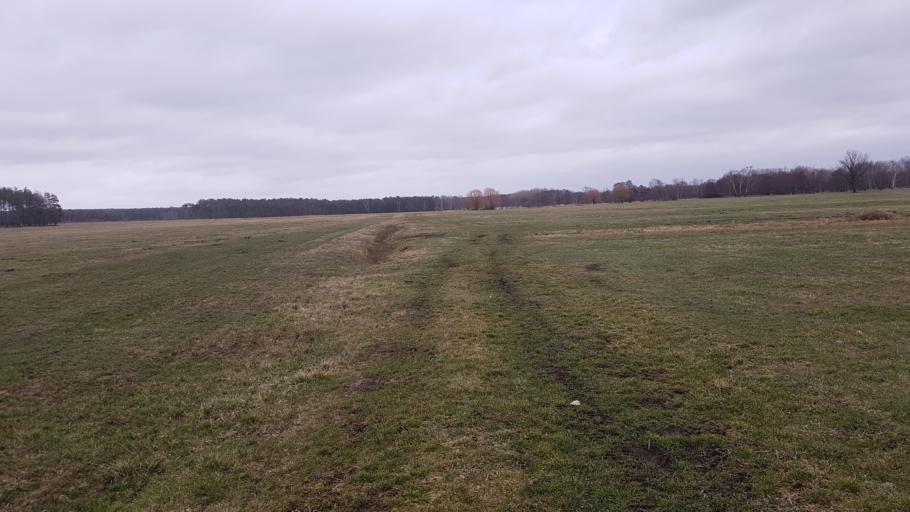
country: DE
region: Brandenburg
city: Schilda
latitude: 51.5969
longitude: 13.3901
